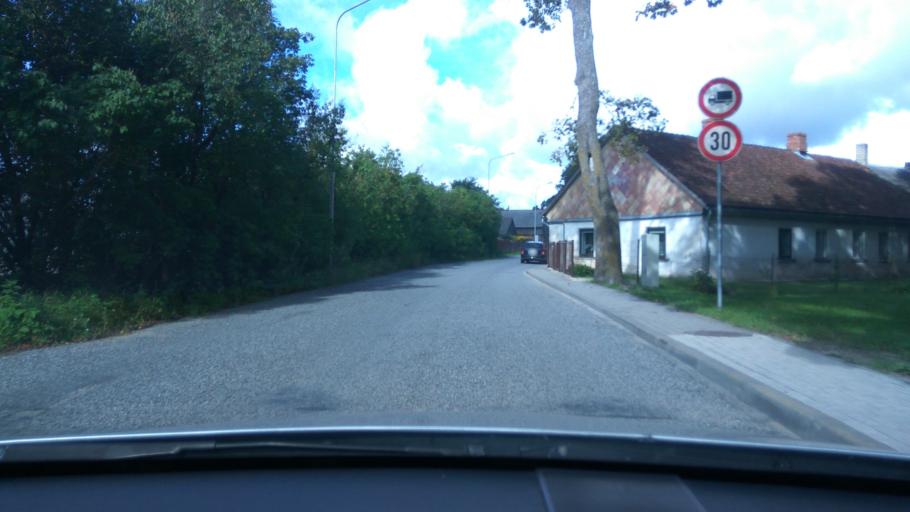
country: LV
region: Kuldigas Rajons
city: Kuldiga
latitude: 56.9688
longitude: 21.9520
